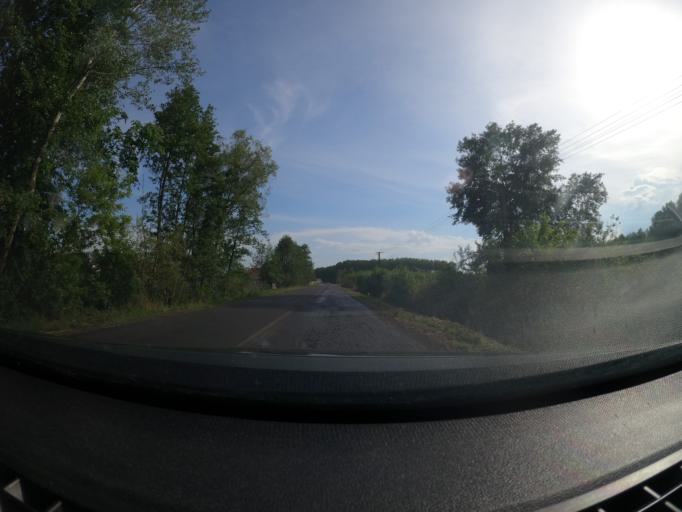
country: HU
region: Hajdu-Bihar
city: Nyirabrany
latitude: 47.5276
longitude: 21.9850
